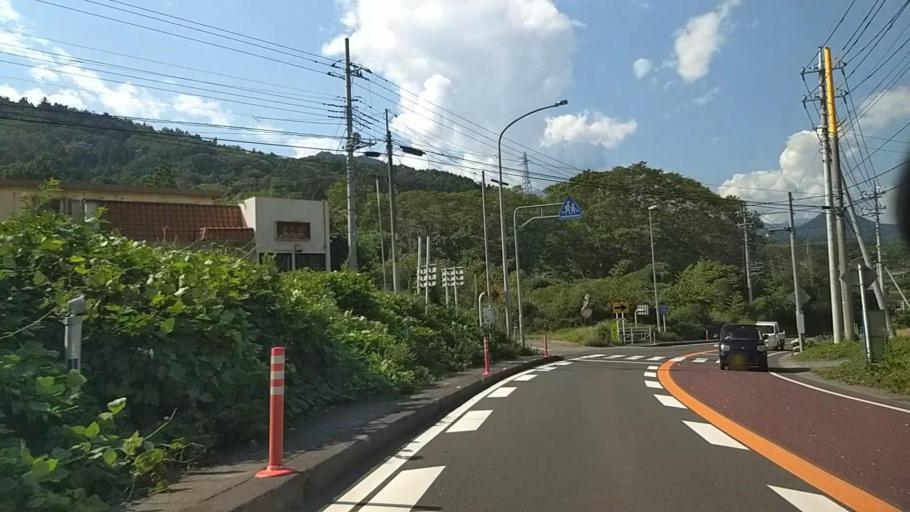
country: JP
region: Yamanashi
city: Ryuo
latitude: 35.4042
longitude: 138.4421
